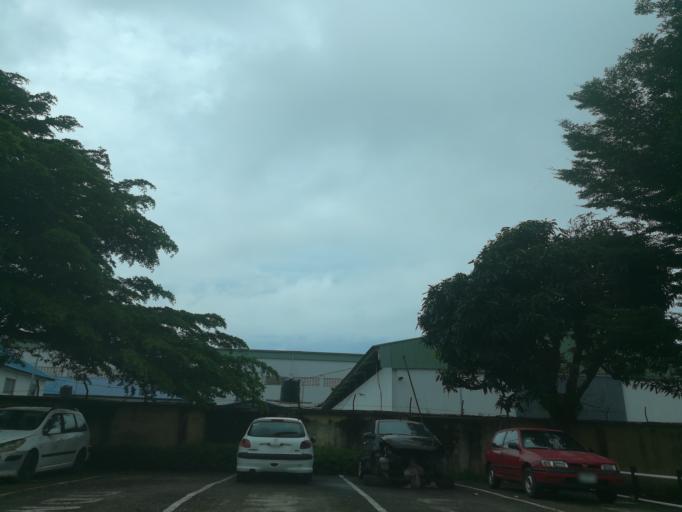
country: NG
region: Lagos
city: Lagos
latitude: 6.4239
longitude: 3.4088
